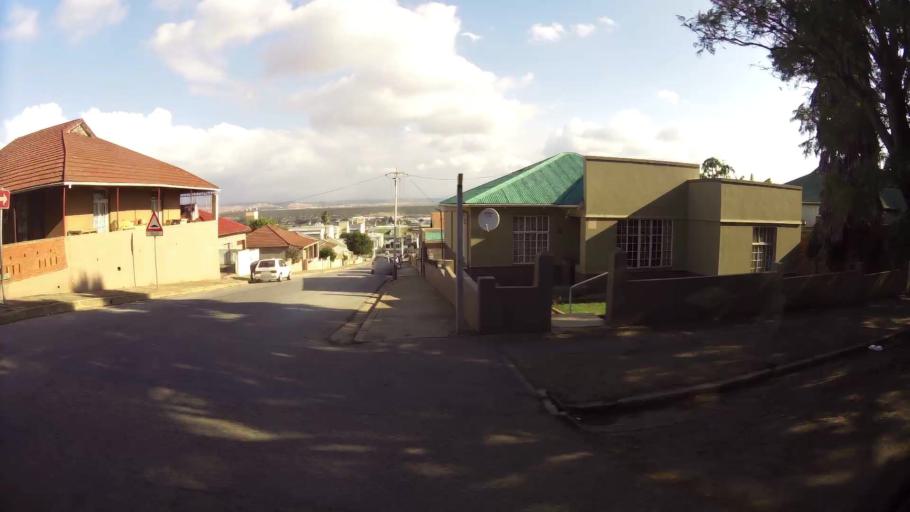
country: ZA
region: Eastern Cape
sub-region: Nelson Mandela Bay Metropolitan Municipality
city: Uitenhage
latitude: -33.7657
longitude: 25.4024
